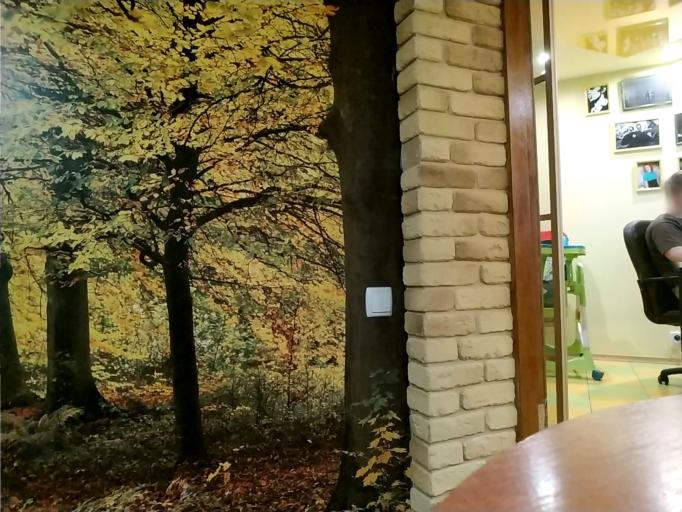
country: RU
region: Tverskaya
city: Zapadnaya Dvina
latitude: 56.3316
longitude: 31.8853
